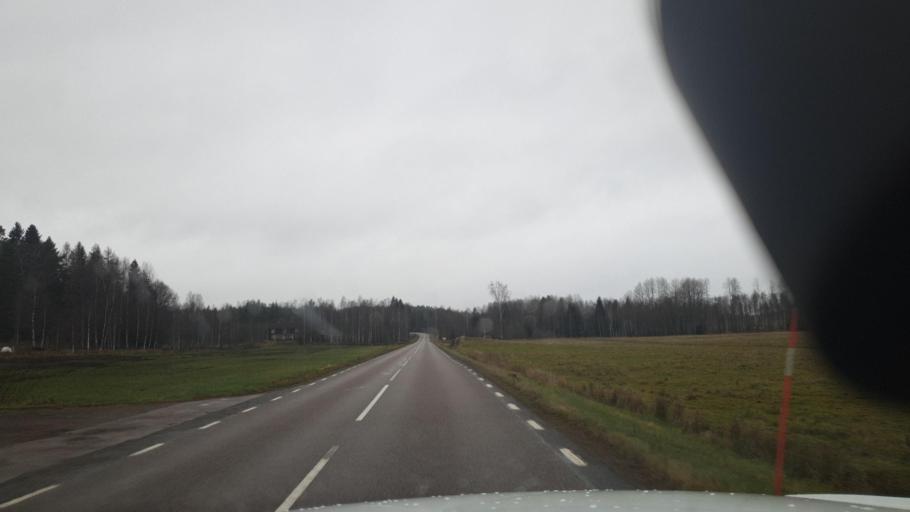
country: SE
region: Vaermland
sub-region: Arvika Kommun
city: Arvika
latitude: 59.4991
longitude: 12.6845
